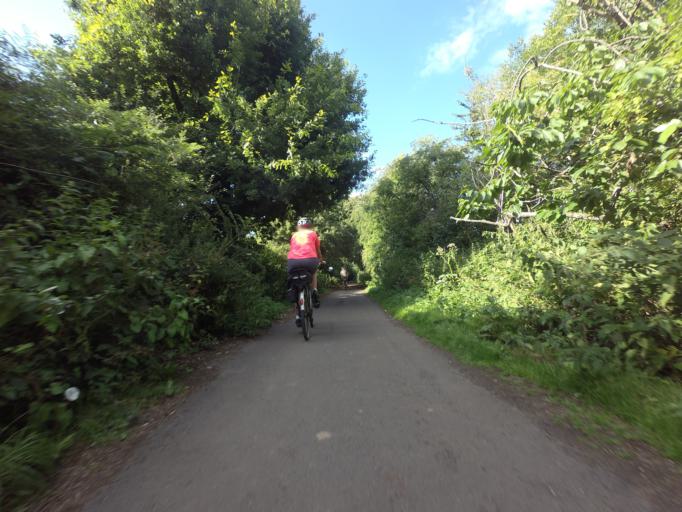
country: GB
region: England
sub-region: East Sussex
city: Hailsham
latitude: 50.8866
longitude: 0.2517
